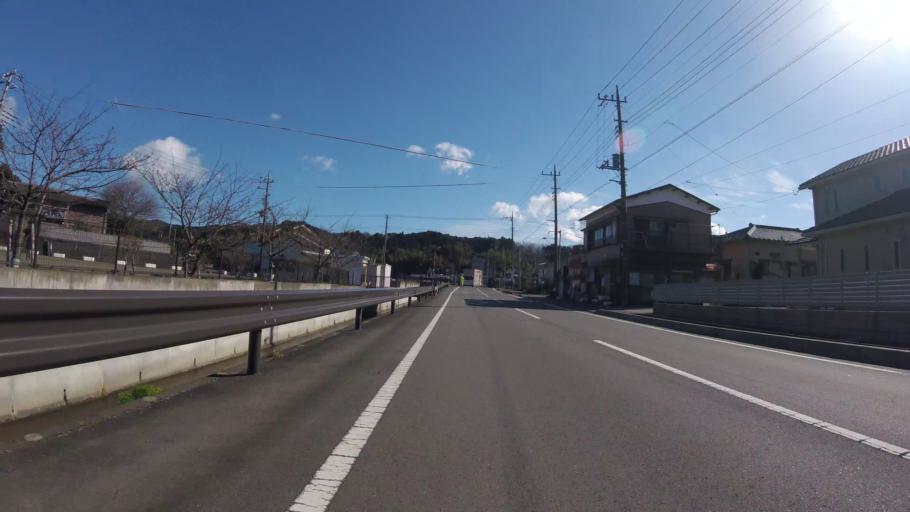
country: JP
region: Shizuoka
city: Atami
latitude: 35.0285
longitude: 139.0094
